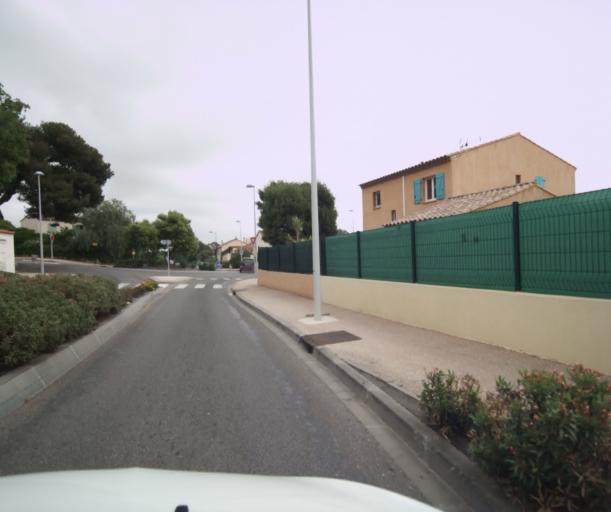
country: FR
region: Provence-Alpes-Cote d'Azur
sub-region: Departement du Var
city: La Garde
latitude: 43.1238
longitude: 6.0000
